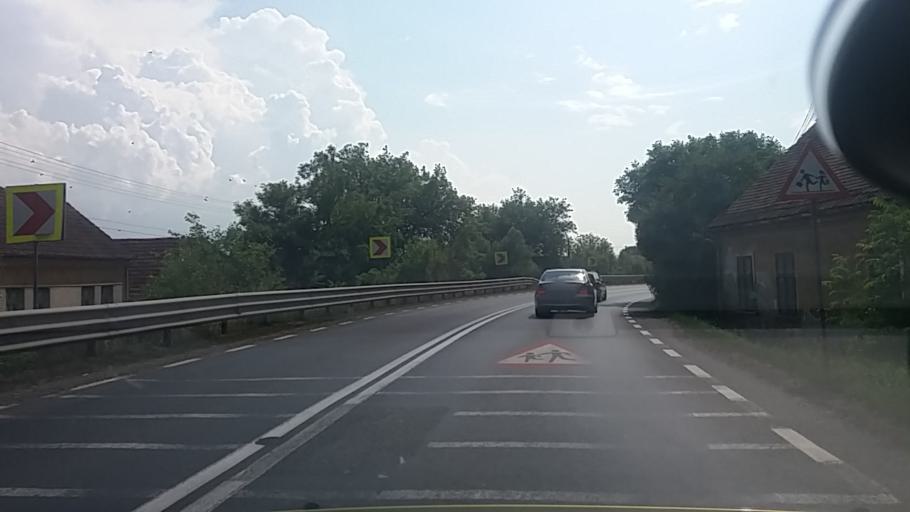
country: RO
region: Arad
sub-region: Comuna Varadia de Mures
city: Varadia de Mures
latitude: 46.0334
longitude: 22.0934
